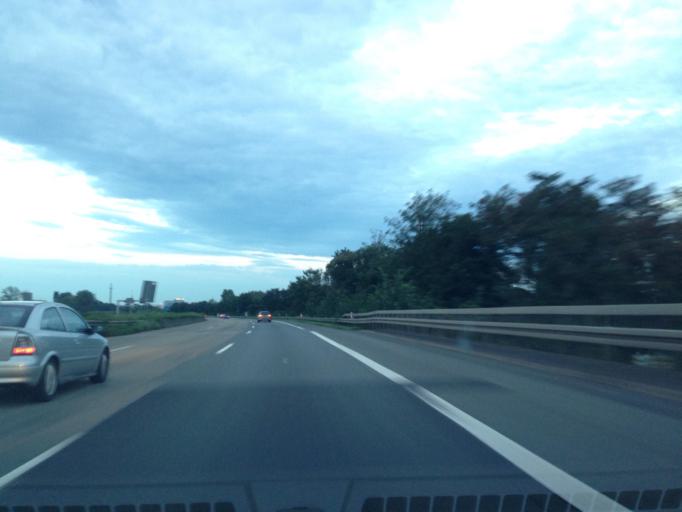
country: DE
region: North Rhine-Westphalia
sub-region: Regierungsbezirk Dusseldorf
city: Hochfeld
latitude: 51.4353
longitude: 6.7377
